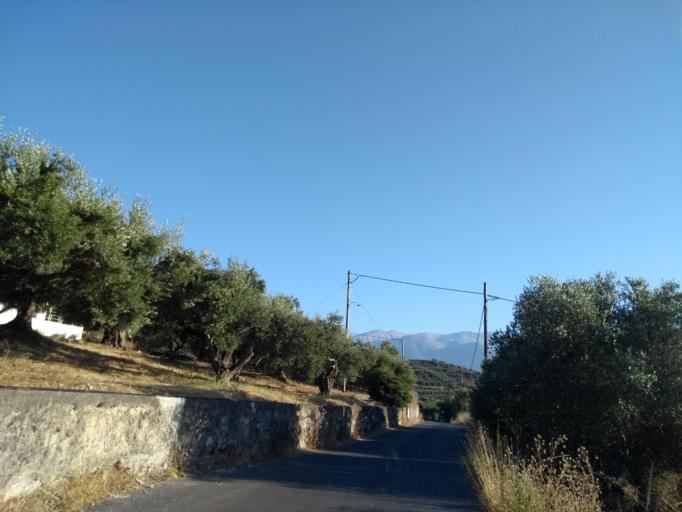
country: GR
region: Crete
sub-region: Nomos Chanias
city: Kalivai
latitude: 35.4445
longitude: 24.1722
